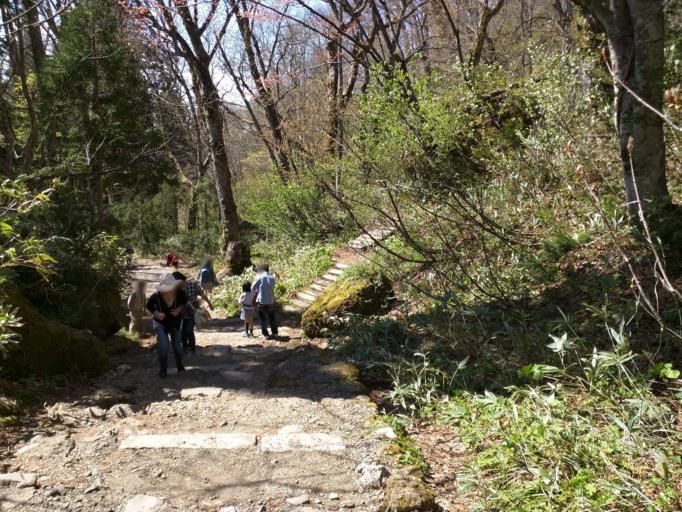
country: JP
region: Nagano
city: Nagano-shi
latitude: 36.7652
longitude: 138.0628
